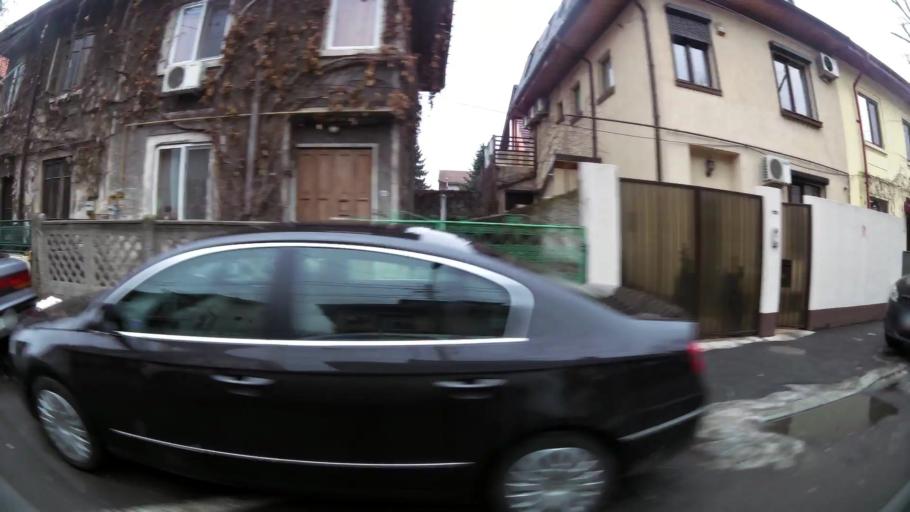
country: RO
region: Bucuresti
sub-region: Municipiul Bucuresti
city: Bucuresti
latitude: 44.4644
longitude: 26.0647
